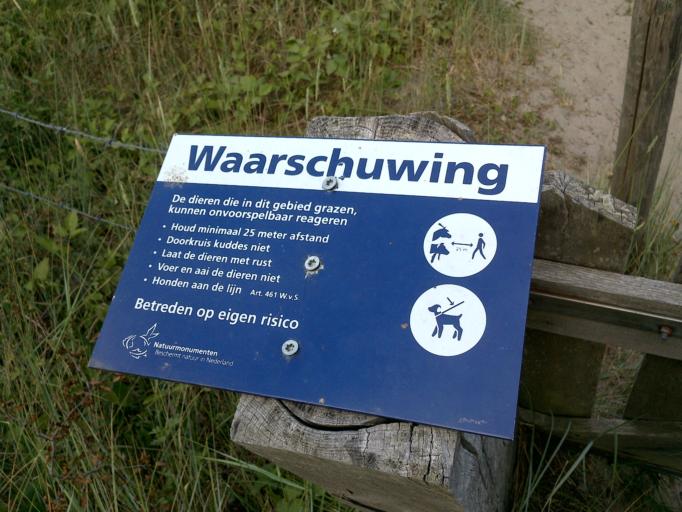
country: NL
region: South Holland
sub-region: Gemeente Goeree-Overflakkee
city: Goedereede
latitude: 51.8903
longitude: 4.0356
